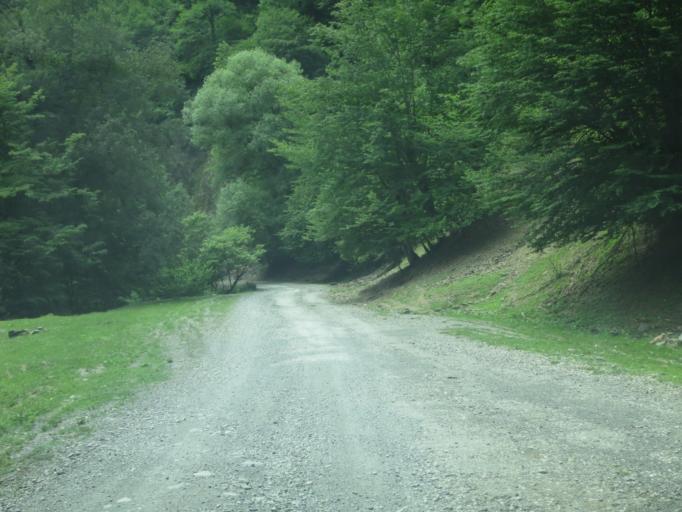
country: GE
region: Kakheti
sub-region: Telavi
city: Telavi
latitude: 42.1841
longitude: 45.4400
